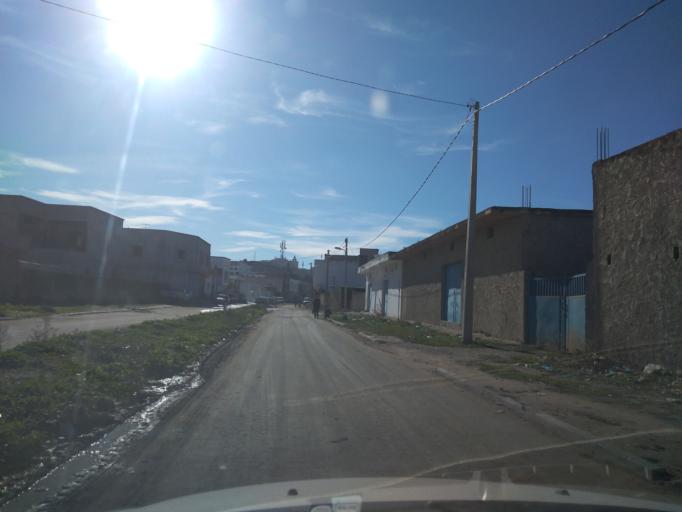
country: TN
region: Ariana
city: Qal'at al Andalus
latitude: 37.0654
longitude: 10.1199
